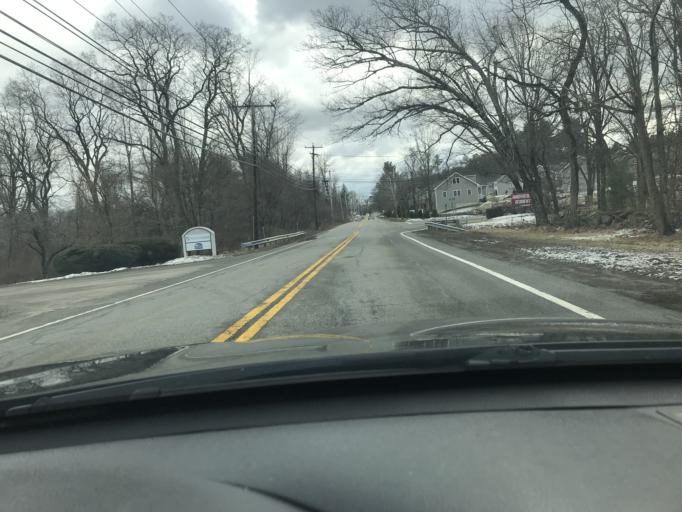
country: US
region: Massachusetts
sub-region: Middlesex County
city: Tyngsboro
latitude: 42.6612
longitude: -71.4071
